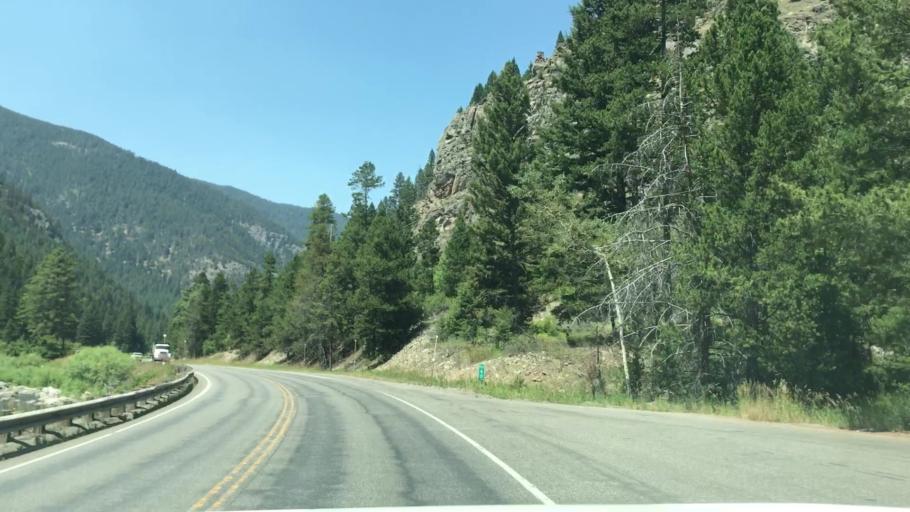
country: US
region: Montana
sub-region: Gallatin County
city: Big Sky
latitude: 45.3951
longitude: -111.2069
